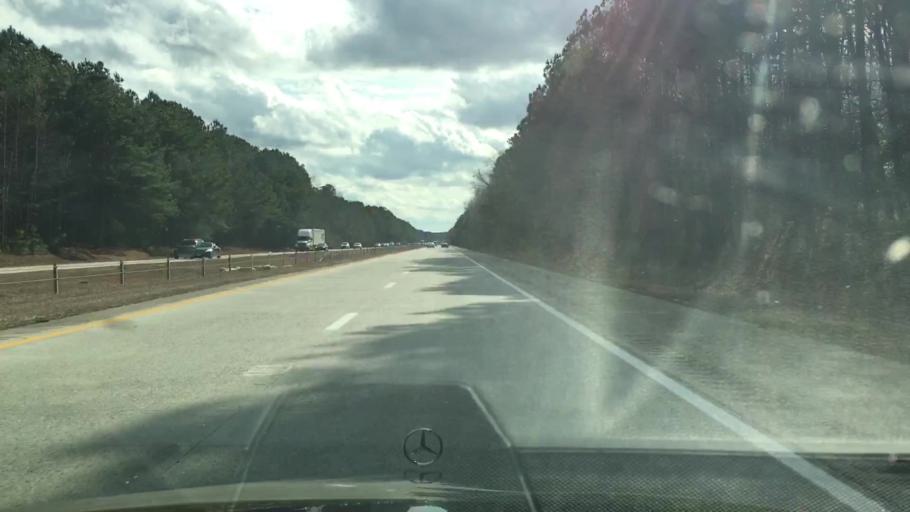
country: US
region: North Carolina
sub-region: Johnston County
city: Benson
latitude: 35.5023
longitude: -78.5546
